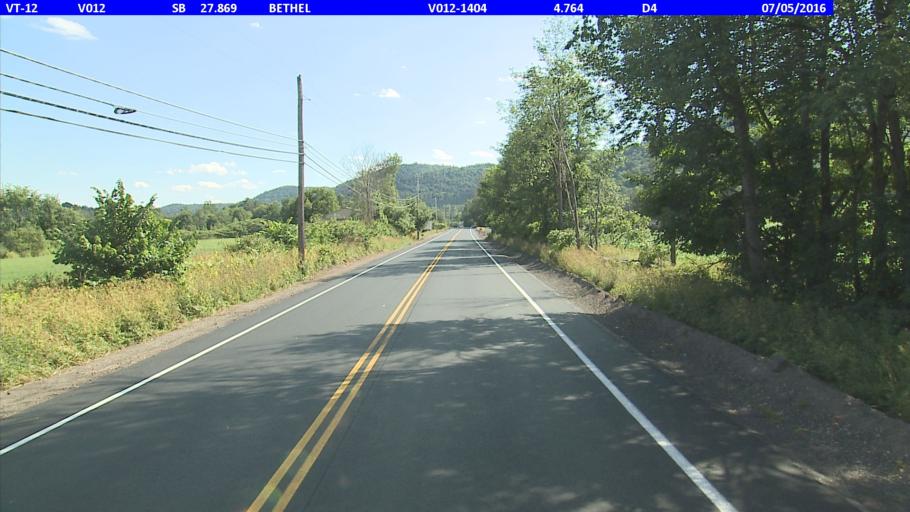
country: US
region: Vermont
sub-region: Orange County
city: Randolph
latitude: 43.8653
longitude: -72.6460
